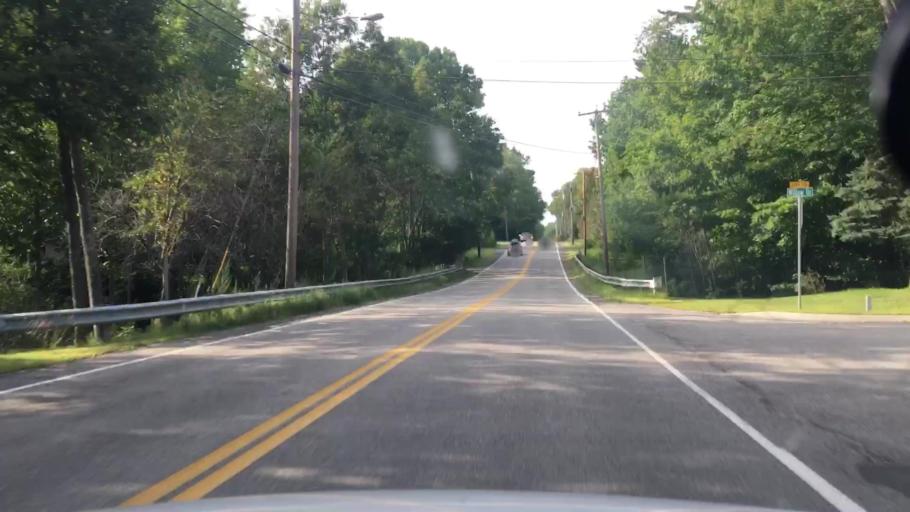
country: US
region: Maine
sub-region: Cumberland County
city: Westbrook
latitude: 43.7328
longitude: -70.3456
